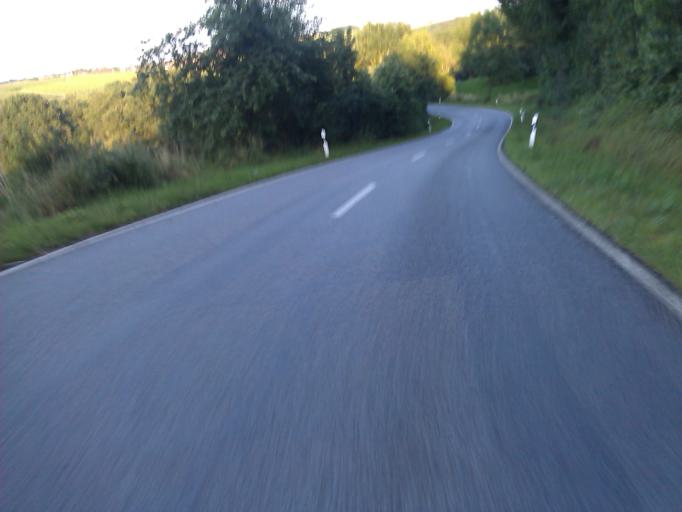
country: DE
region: Baden-Wuerttemberg
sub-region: Regierungsbezirk Stuttgart
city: Talheim
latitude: 49.0673
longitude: 9.1992
